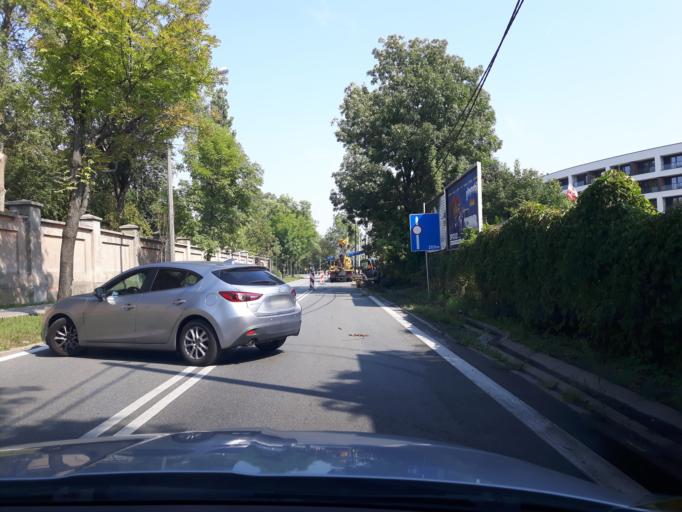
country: PL
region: Masovian Voivodeship
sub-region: Warszawa
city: Targowek
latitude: 52.2803
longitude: 21.0459
